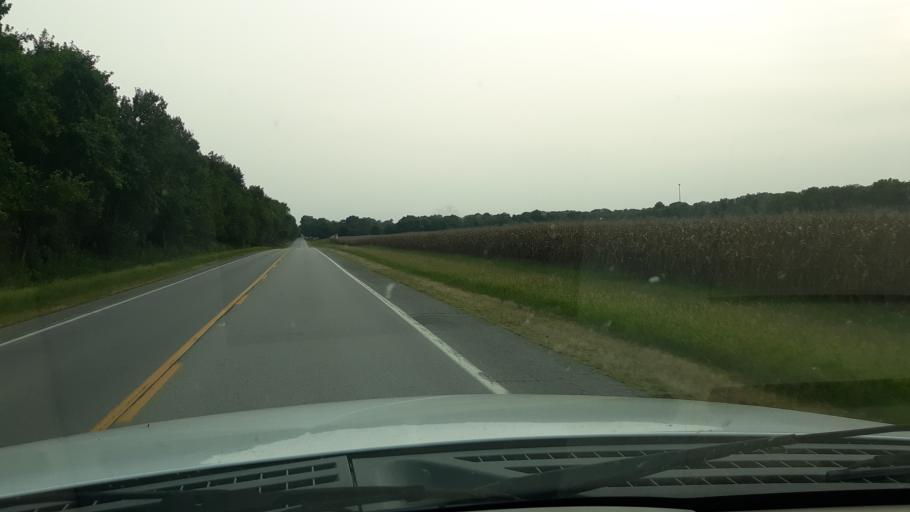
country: US
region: Illinois
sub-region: Edwards County
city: Grayville
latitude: 38.1724
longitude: -88.0550
